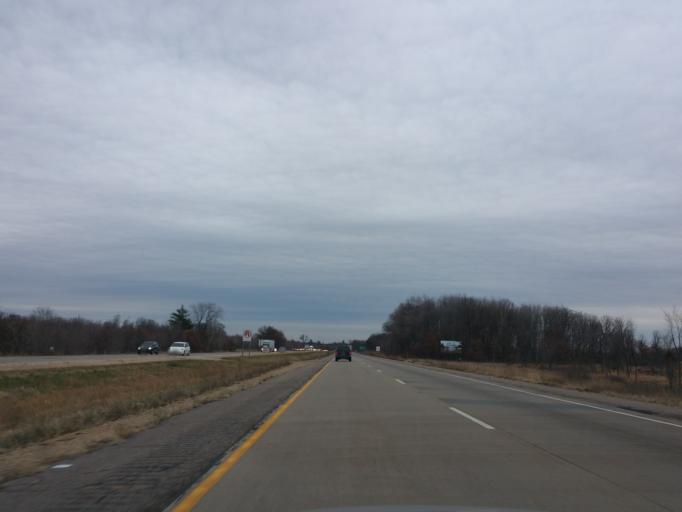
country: US
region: Wisconsin
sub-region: Juneau County
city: New Lisbon
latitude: 43.8787
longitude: -90.1392
